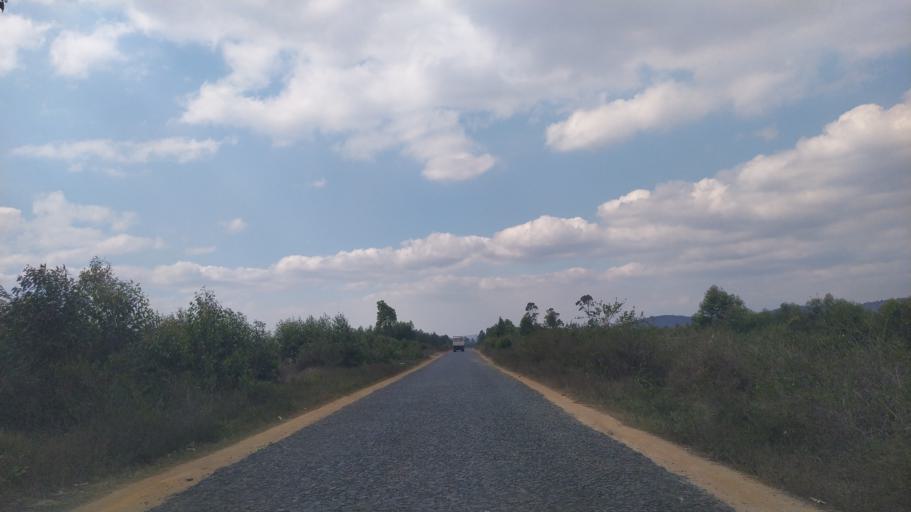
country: MG
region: Alaotra Mangoro
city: Moramanga
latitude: -18.7722
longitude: 48.2507
